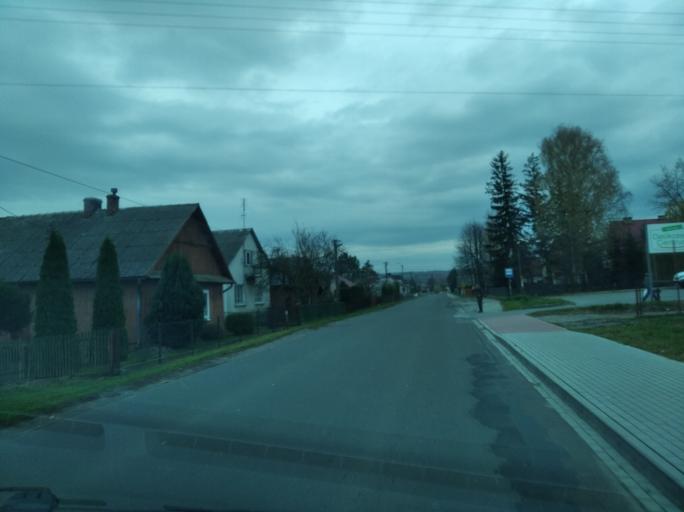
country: PL
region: Subcarpathian Voivodeship
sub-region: Powiat ropczycko-sedziszowski
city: Iwierzyce
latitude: 50.0141
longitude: 21.7525
